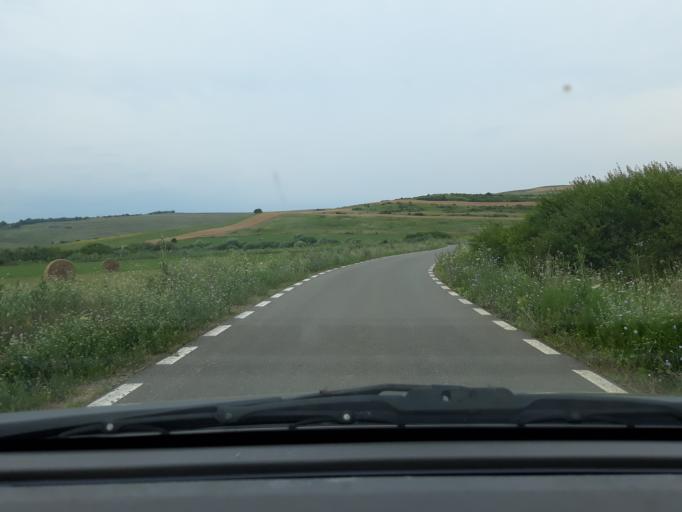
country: RO
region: Salaj
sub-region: Comuna Criseni
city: Criseni
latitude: 47.2735
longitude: 23.0740
